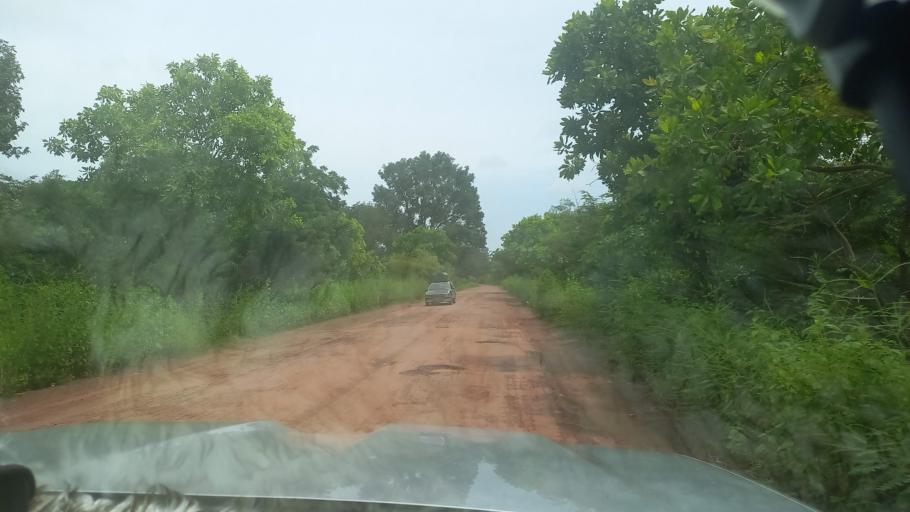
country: SN
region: Kolda
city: Marsassoum
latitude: 12.9042
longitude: -16.0197
